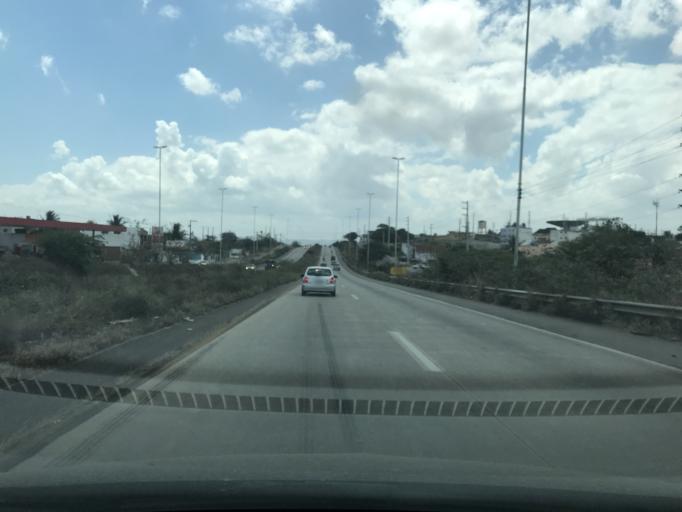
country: BR
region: Pernambuco
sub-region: Caruaru
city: Caruaru
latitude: -8.3034
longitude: -35.9750
